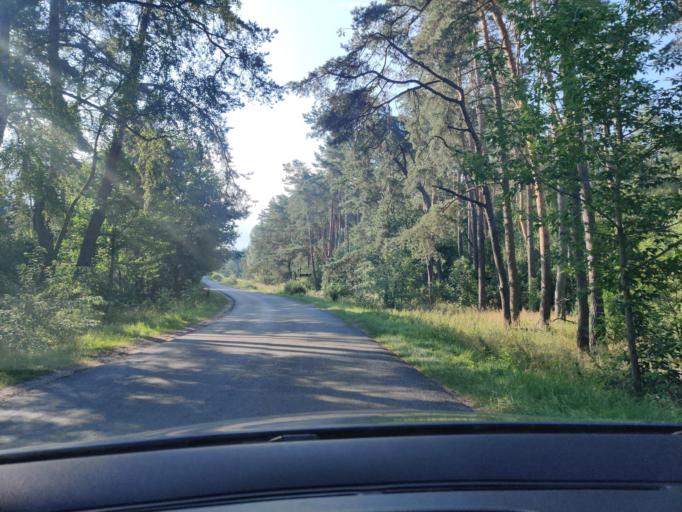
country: PL
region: Greater Poland Voivodeship
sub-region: Powiat koninski
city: Krzymow
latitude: 52.1773
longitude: 18.3365
